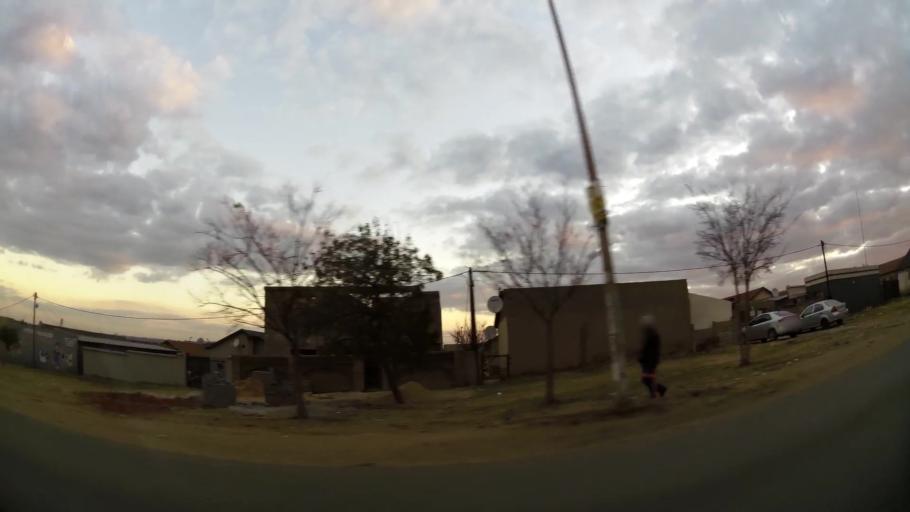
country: ZA
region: Gauteng
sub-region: City of Johannesburg Metropolitan Municipality
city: Midrand
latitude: -25.9869
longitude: 28.1721
